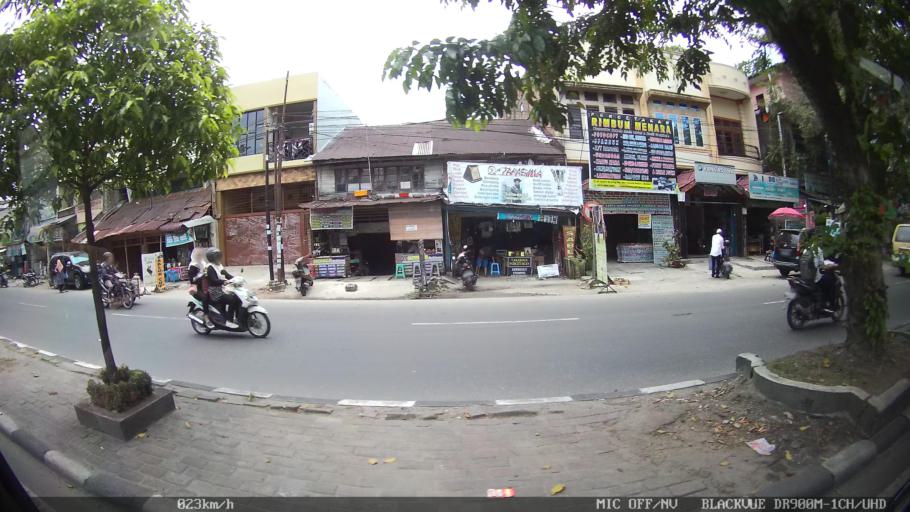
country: ID
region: North Sumatra
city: Medan
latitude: 3.5574
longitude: 98.6629
